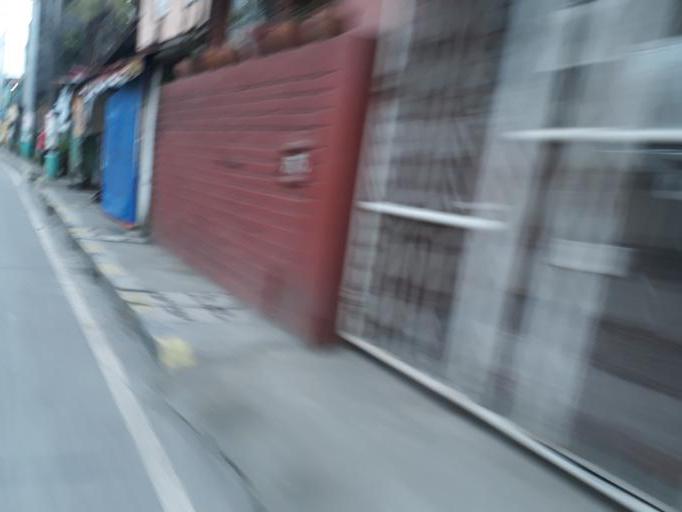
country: PH
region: Calabarzon
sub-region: Province of Rizal
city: Valenzuela
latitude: 14.7050
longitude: 120.9543
